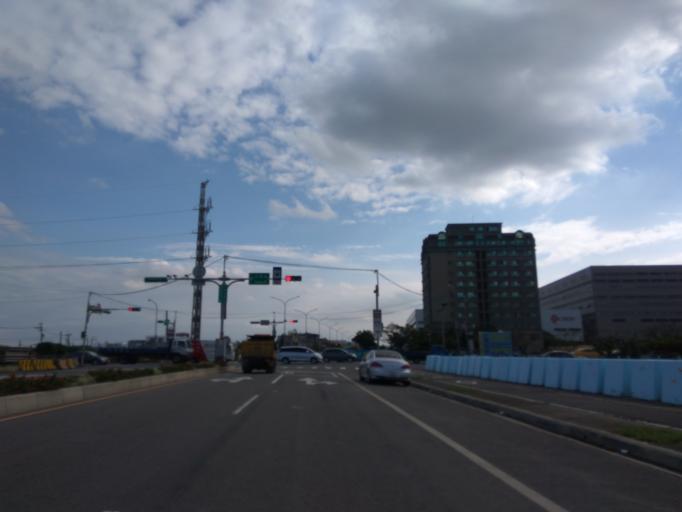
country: TW
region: Taiwan
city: Taoyuan City
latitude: 25.0633
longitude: 121.1770
